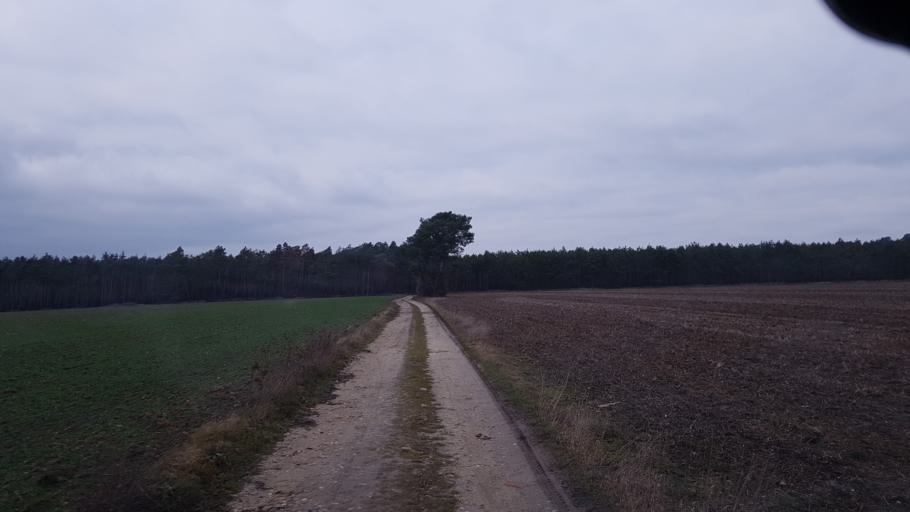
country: DE
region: Brandenburg
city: Finsterwalde
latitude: 51.6149
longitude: 13.6497
